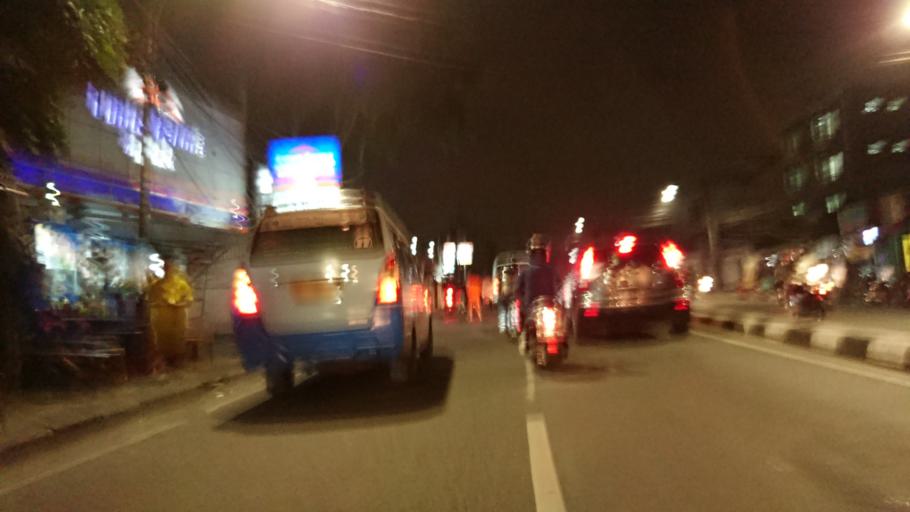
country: ID
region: Jakarta Raya
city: Jakarta
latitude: -6.1919
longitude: 106.8057
